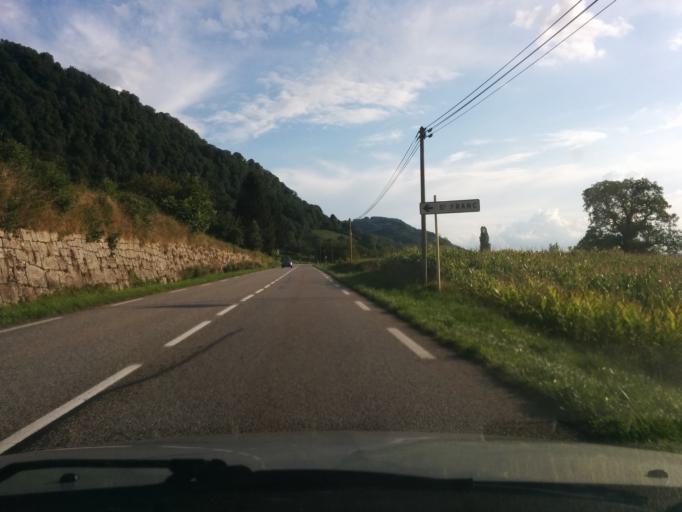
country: FR
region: Rhone-Alpes
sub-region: Departement de la Savoie
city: Saint-Beron
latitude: 45.4964
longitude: 5.7290
